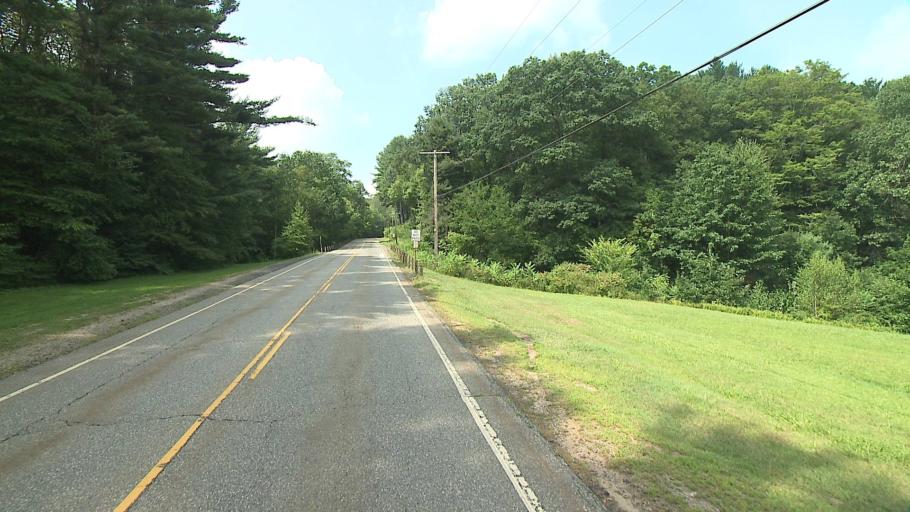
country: US
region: Connecticut
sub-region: Litchfield County
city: Bethlehem Village
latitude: 41.6731
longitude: -73.1440
